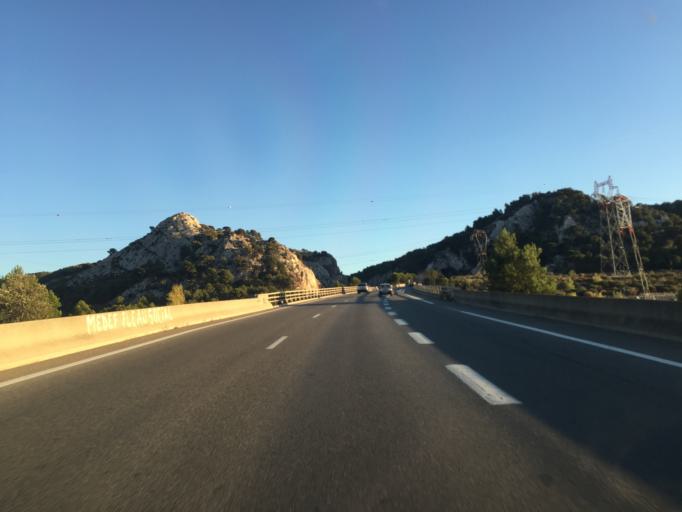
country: FR
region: Provence-Alpes-Cote d'Azur
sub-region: Departement des Bouches-du-Rhone
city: Les Pennes-Mirabeau
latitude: 43.4016
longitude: 5.2982
